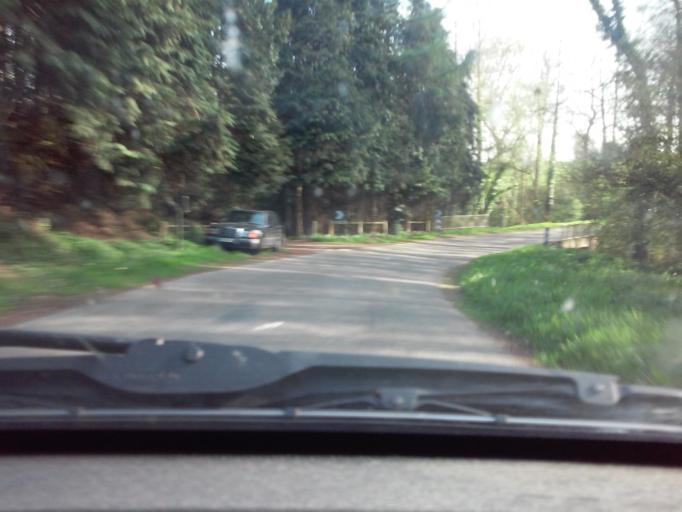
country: FR
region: Brittany
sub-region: Departement d'Ille-et-Vilaine
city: Javene
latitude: 48.3110
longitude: -1.2455
